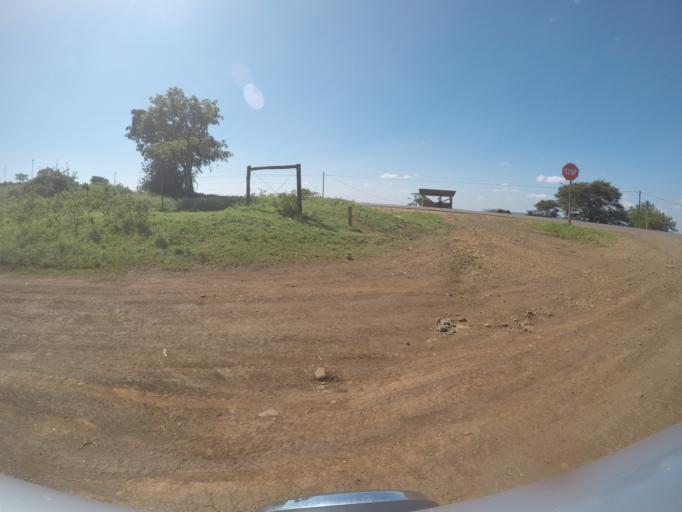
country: ZA
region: KwaZulu-Natal
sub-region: uThungulu District Municipality
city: Empangeni
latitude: -28.5625
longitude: 31.7033
